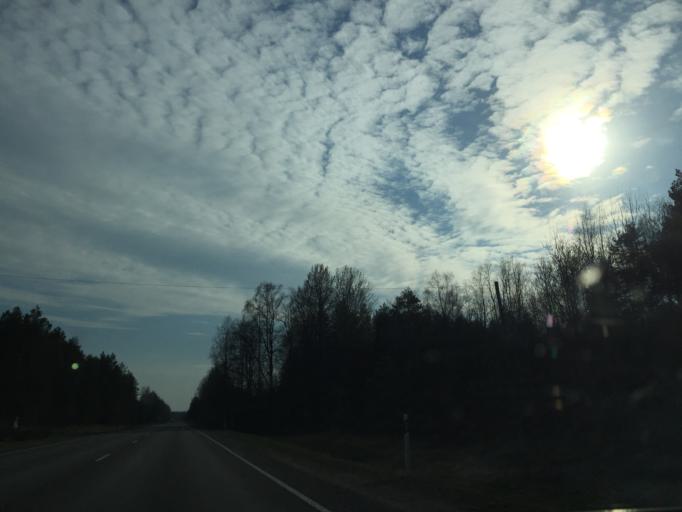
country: EE
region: Ida-Virumaa
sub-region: Kohtla-Nomme vald
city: Kohtla-Nomme
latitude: 59.0345
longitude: 27.2416
